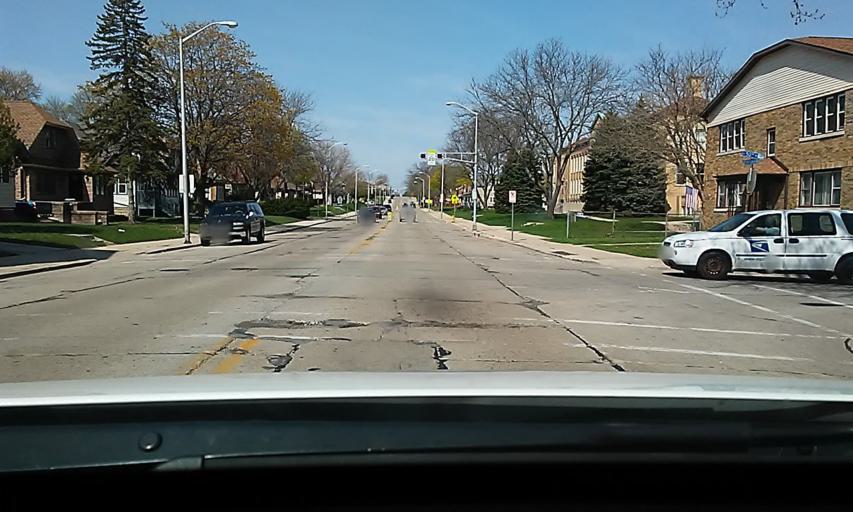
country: US
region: Wisconsin
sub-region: Milwaukee County
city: West Milwaukee
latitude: 43.0169
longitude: -87.9758
